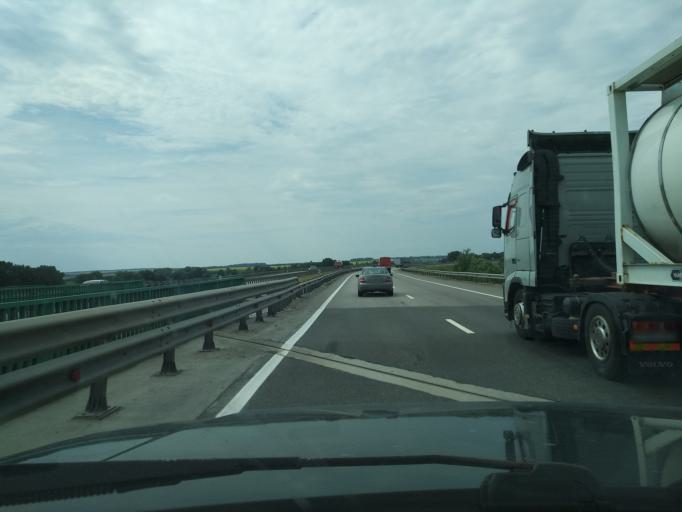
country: RU
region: Lipetsk
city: Khlevnoye
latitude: 52.0586
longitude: 39.1866
